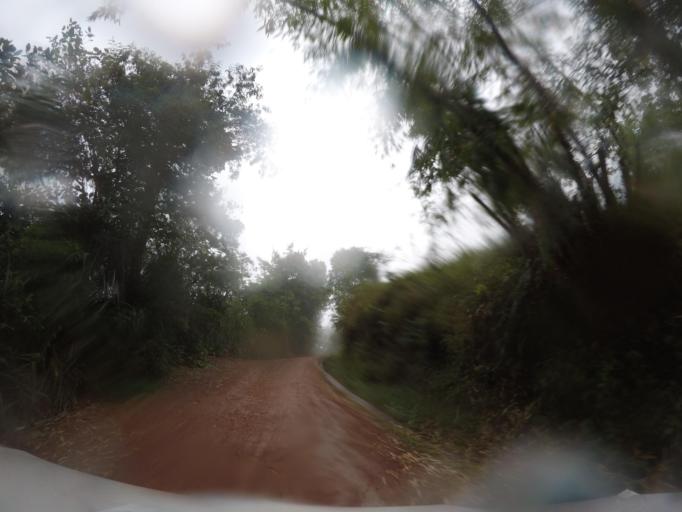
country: TL
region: Baucau
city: Venilale
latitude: -8.6381
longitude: 126.4142
